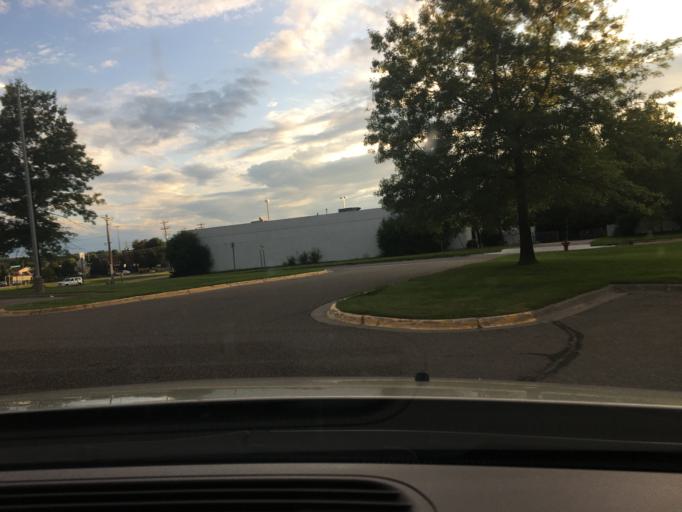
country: US
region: Minnesota
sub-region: Dakota County
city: West Saint Paul
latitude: 44.8987
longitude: -93.0779
